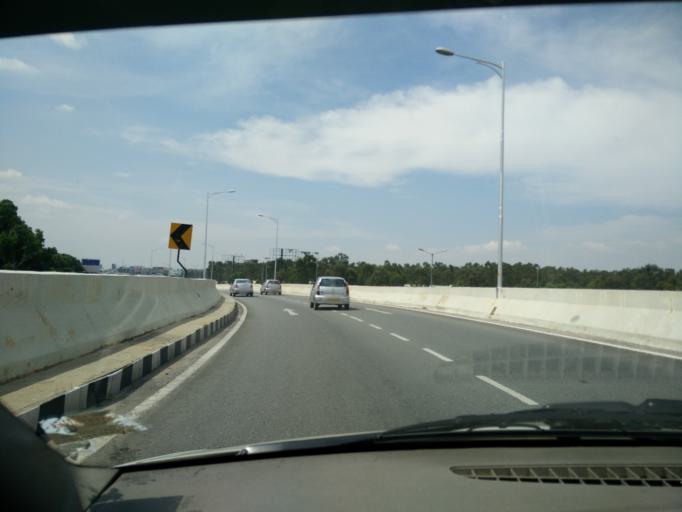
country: IN
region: Karnataka
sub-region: Bangalore Rural
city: Devanhalli
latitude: 13.2002
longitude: 77.6605
